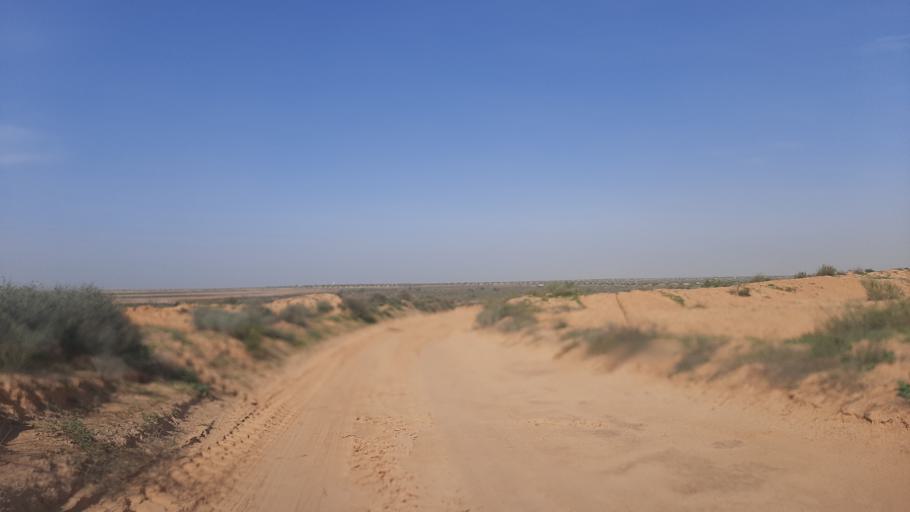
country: TN
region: Madanin
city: Zarzis
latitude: 33.4387
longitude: 10.8070
